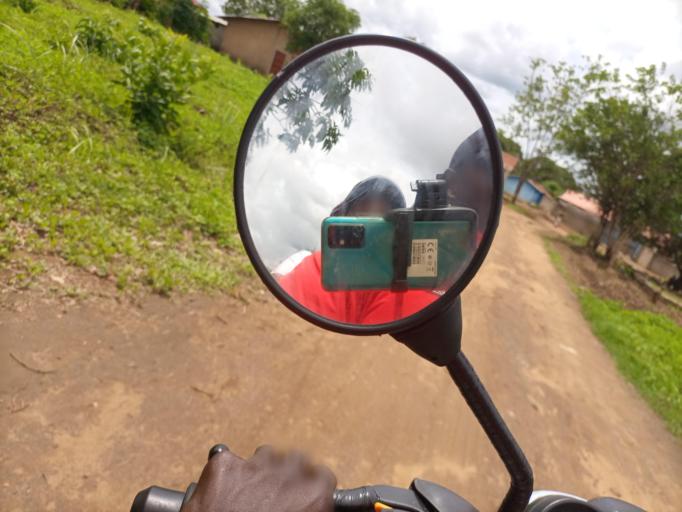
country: SL
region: Southern Province
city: Bo
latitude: 7.9664
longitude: -11.7151
